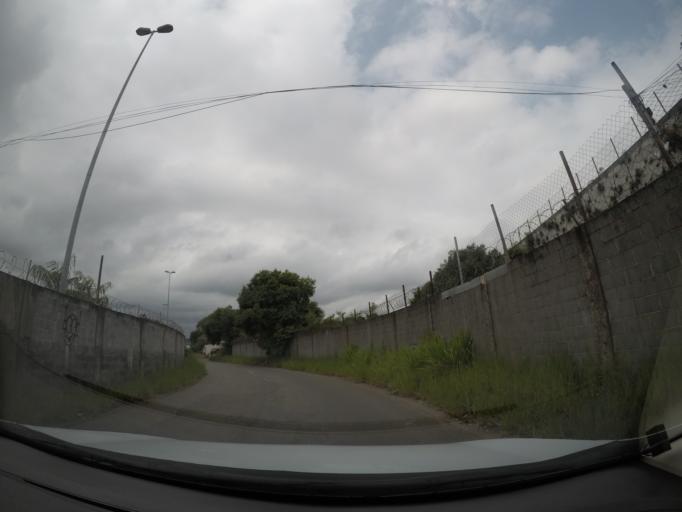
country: BR
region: Sao Paulo
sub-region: Itaquaquecetuba
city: Itaquaquecetuba
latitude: -23.4243
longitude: -46.3977
